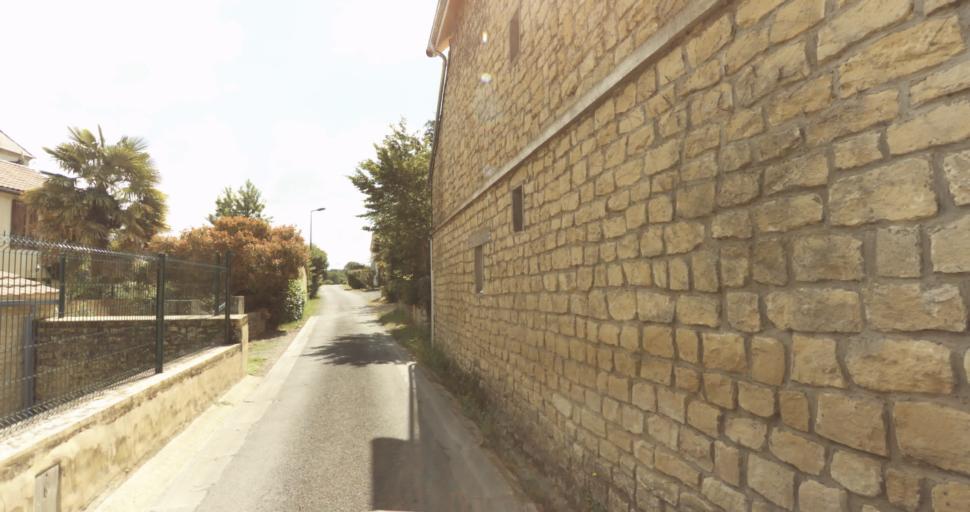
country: FR
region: Aquitaine
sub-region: Departement de la Dordogne
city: Le Bugue
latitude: 44.8414
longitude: 0.9060
